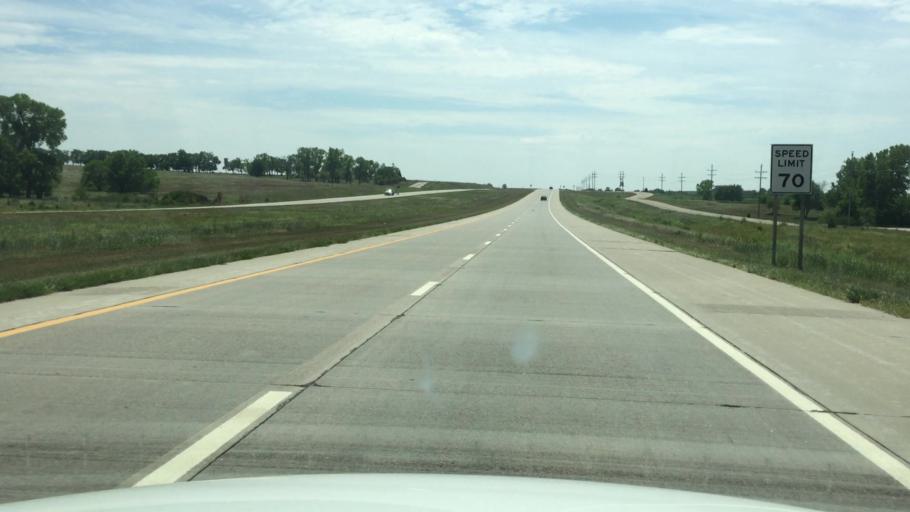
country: US
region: Kansas
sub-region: Shawnee County
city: Silver Lake
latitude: 39.2435
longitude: -95.7197
